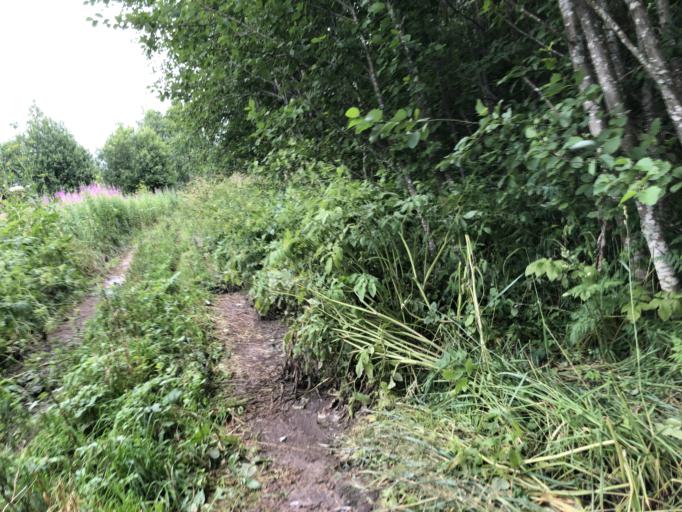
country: RU
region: Tverskaya
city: Rzhev
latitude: 56.2376
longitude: 34.3845
